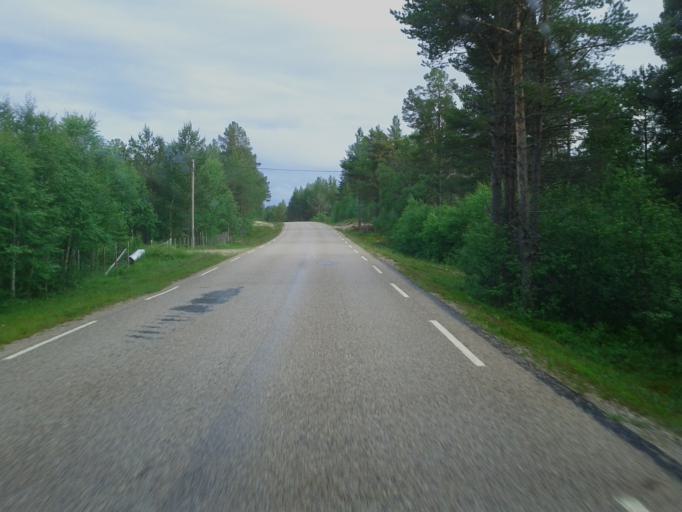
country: NO
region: Hedmark
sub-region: Engerdal
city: Engerdal
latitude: 62.0619
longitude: 11.6797
